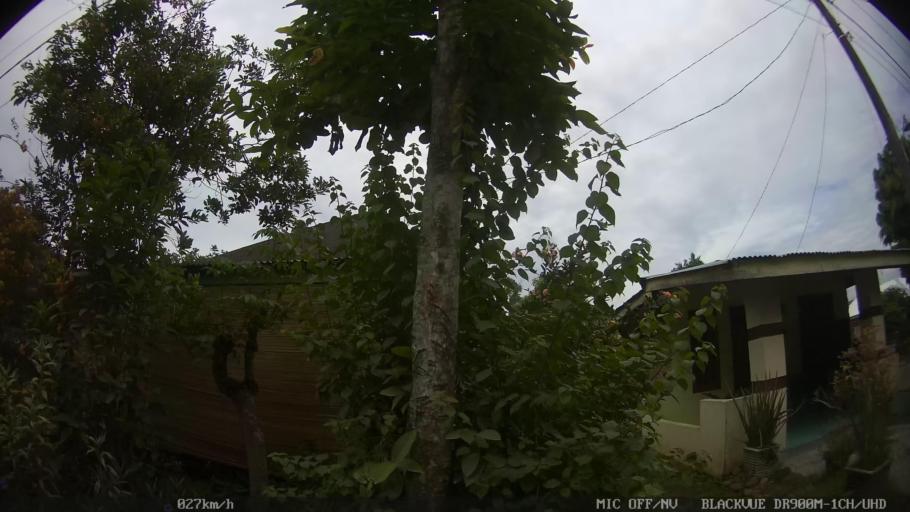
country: ID
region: North Sumatra
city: Sunggal
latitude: 3.6416
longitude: 98.5921
